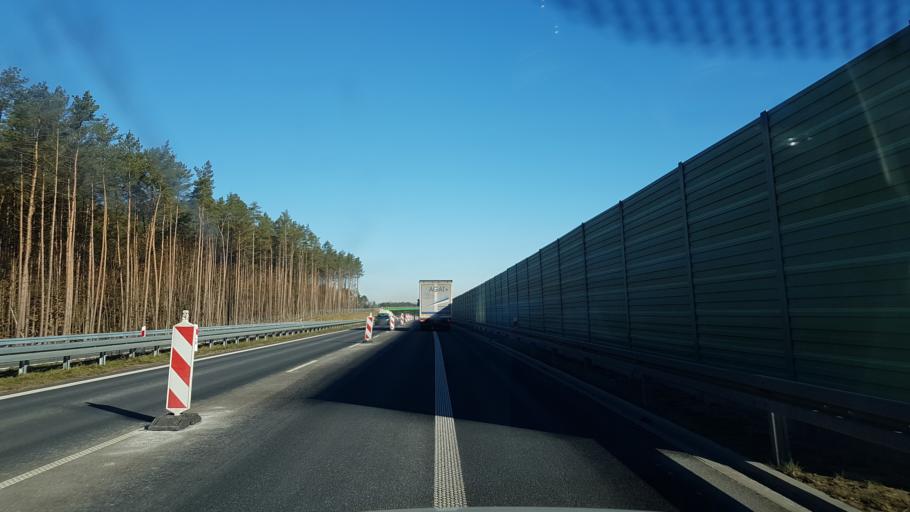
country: PL
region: West Pomeranian Voivodeship
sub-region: Powiat goleniowski
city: Przybiernow
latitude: 53.7335
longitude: 14.7740
